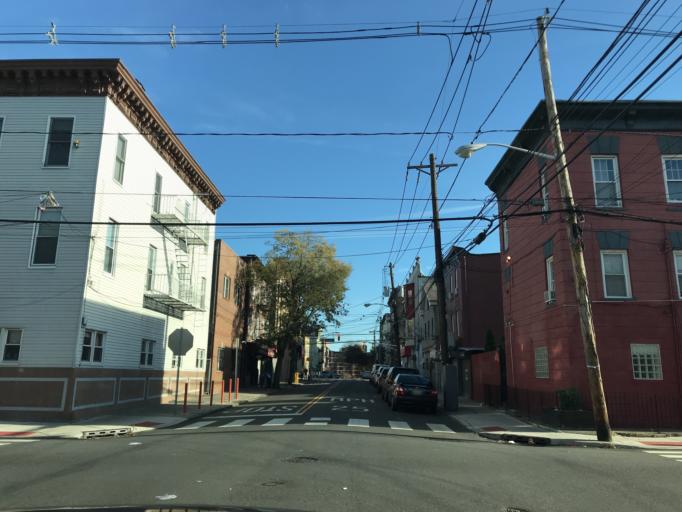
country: US
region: New Jersey
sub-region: Hudson County
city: Hoboken
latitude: 40.7416
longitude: -74.0471
